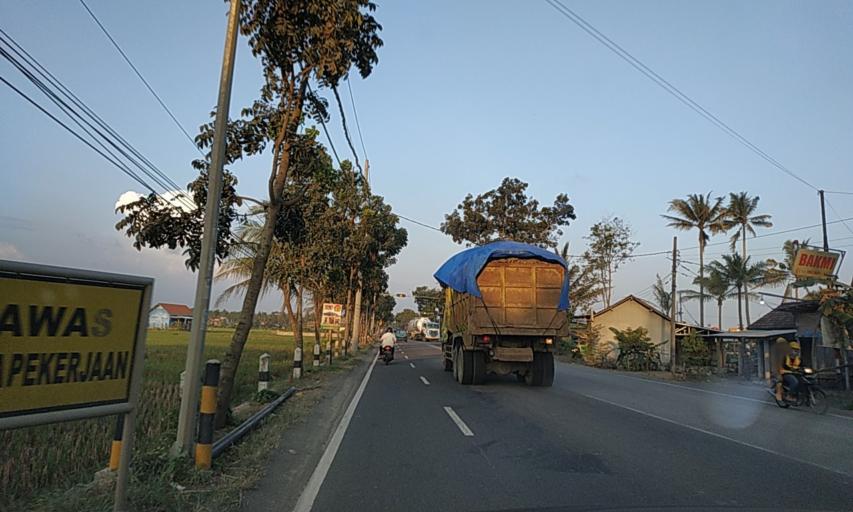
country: ID
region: Daerah Istimewa Yogyakarta
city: Srandakan
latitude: -7.8866
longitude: 110.0584
